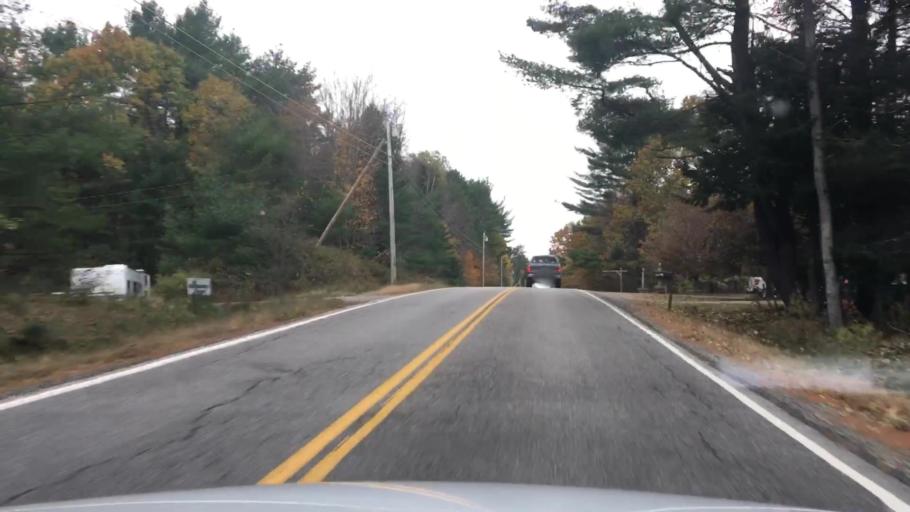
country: US
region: Maine
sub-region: Sagadahoc County
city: Richmond
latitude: 44.1288
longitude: -69.9122
